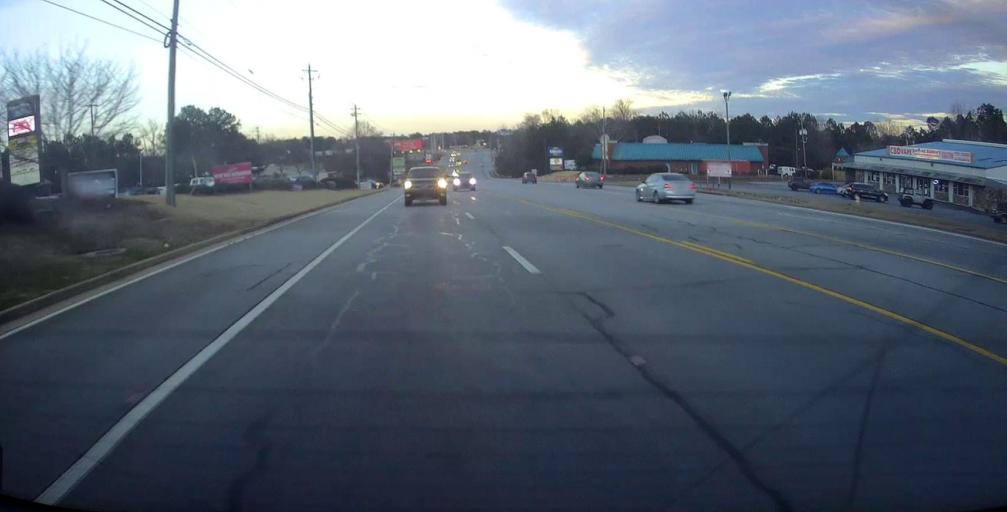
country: US
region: Alabama
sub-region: Russell County
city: Phenix City
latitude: 32.5572
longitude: -84.9443
